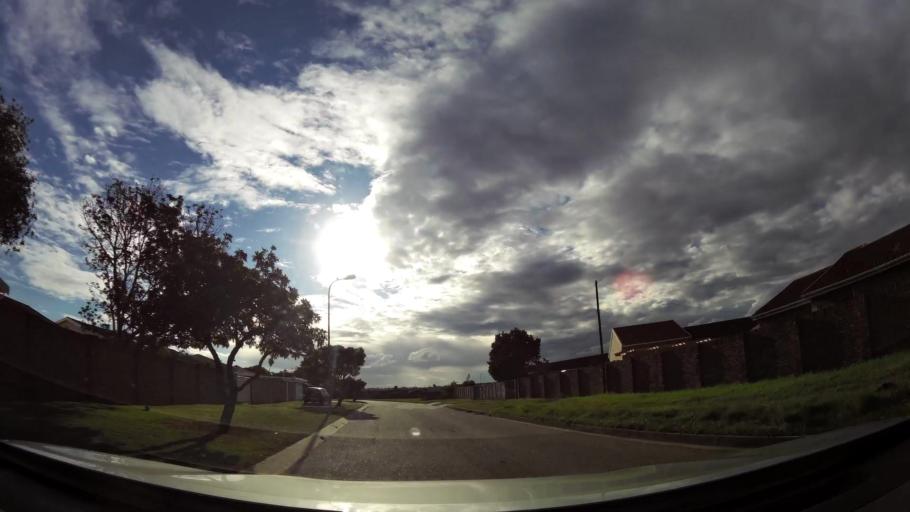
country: ZA
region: Eastern Cape
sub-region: Nelson Mandela Bay Metropolitan Municipality
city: Port Elizabeth
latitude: -33.9524
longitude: 25.4824
